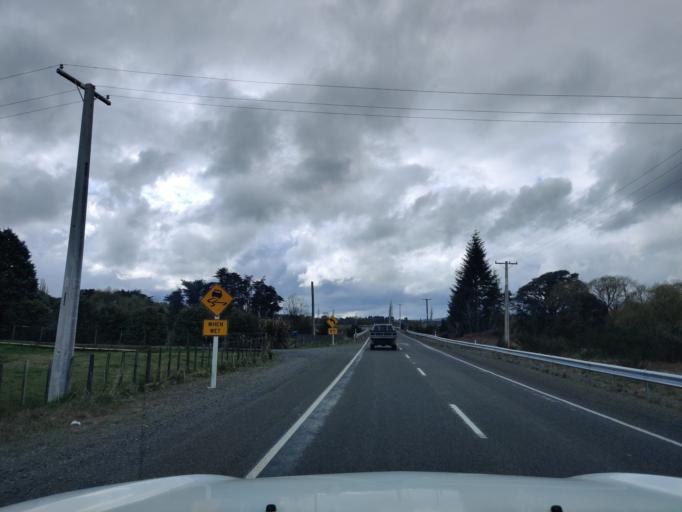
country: NZ
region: Manawatu-Wanganui
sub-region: Ruapehu District
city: Waiouru
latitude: -39.4477
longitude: 175.2915
